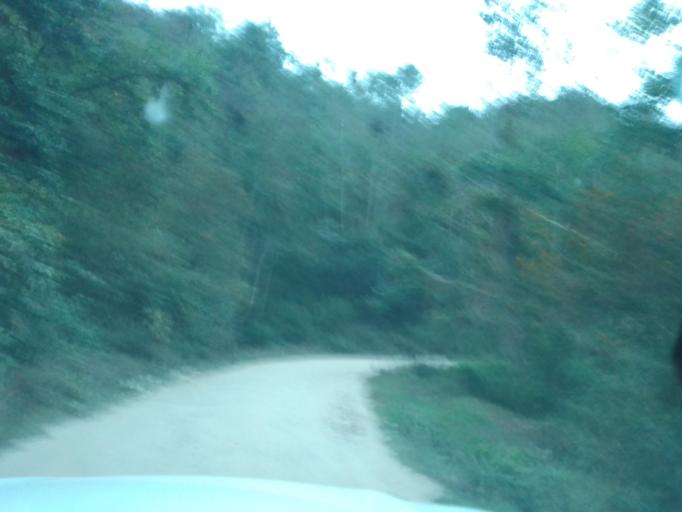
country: MX
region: Chiapas
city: Motozintla de Mendoza
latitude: 15.2185
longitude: -92.2386
